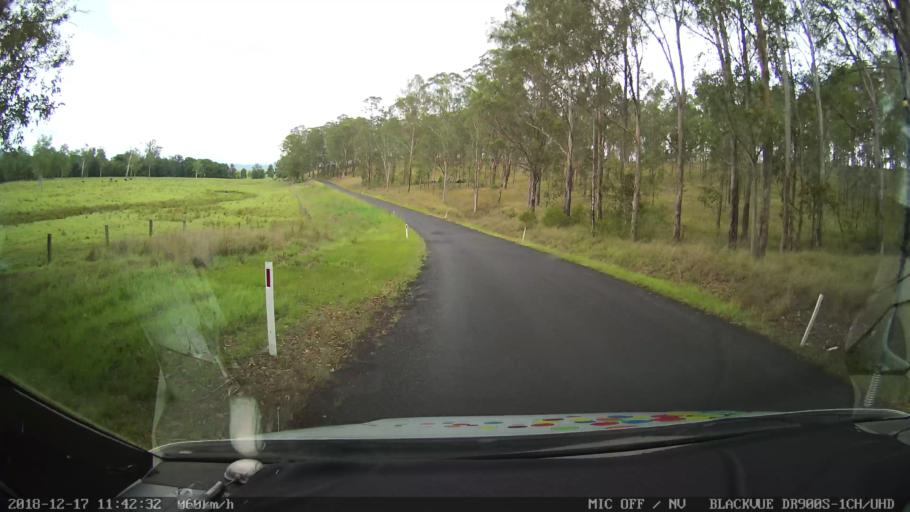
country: AU
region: New South Wales
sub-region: Kyogle
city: Kyogle
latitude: -28.6680
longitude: 152.5919
